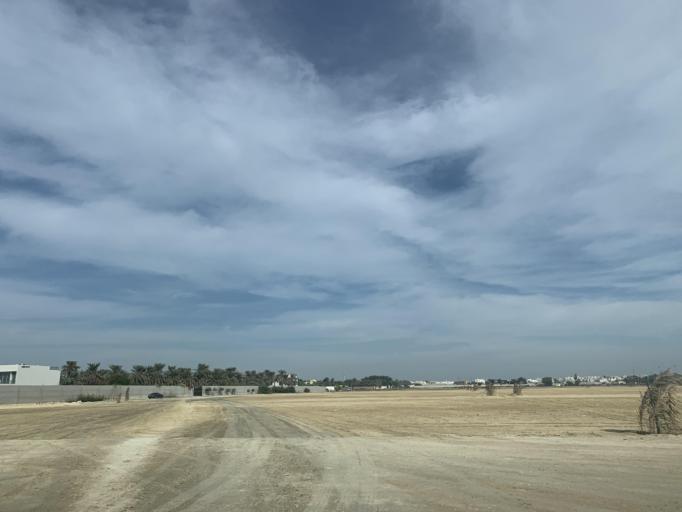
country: BH
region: Central Governorate
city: Madinat Hamad
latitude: 26.1170
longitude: 50.4633
